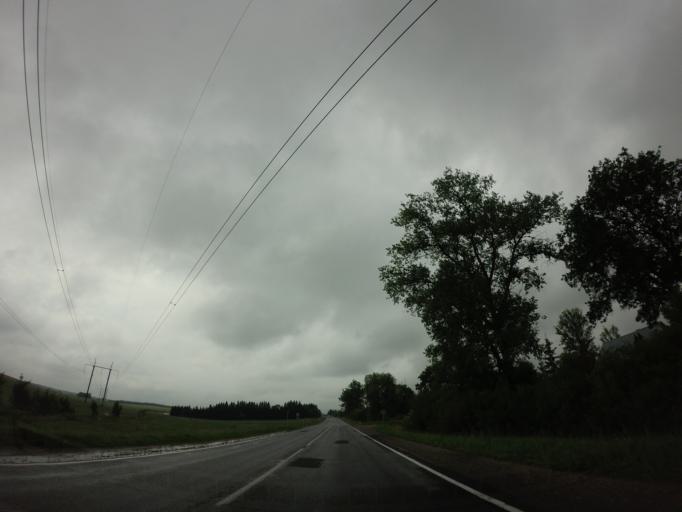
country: LT
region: Alytaus apskritis
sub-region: Alytus
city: Alytus
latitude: 54.3555
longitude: 23.9721
